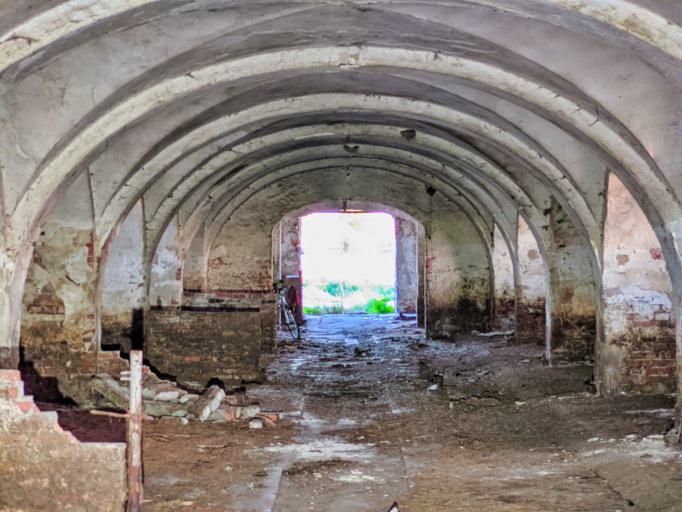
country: PL
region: Lubusz
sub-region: Powiat zaganski
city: Ilowa
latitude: 51.5442
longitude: 15.1975
